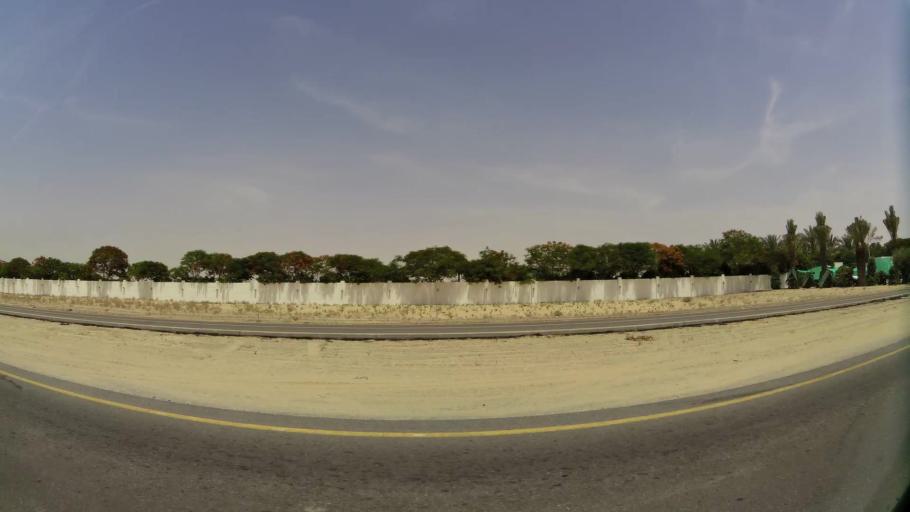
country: AE
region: Ash Shariqah
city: Sharjah
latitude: 25.2453
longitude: 55.4786
